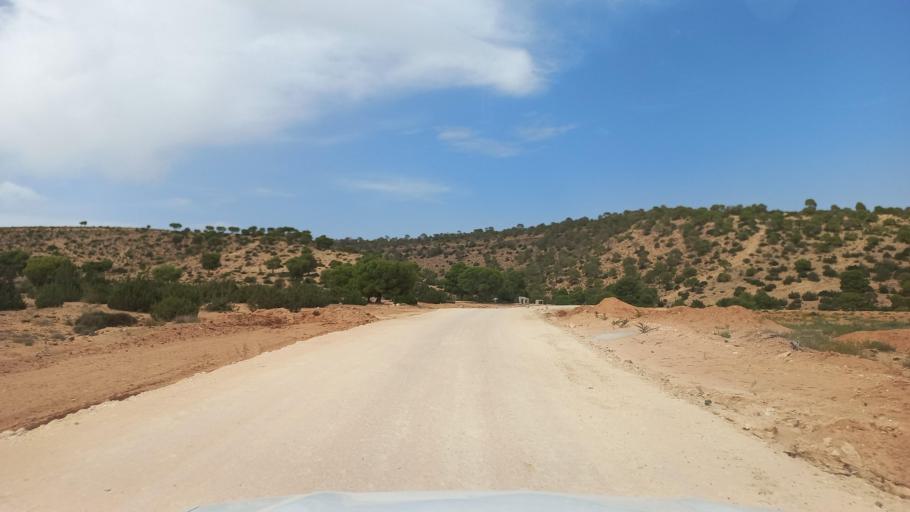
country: TN
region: Al Qasrayn
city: Kasserine
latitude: 35.3725
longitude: 8.8880
